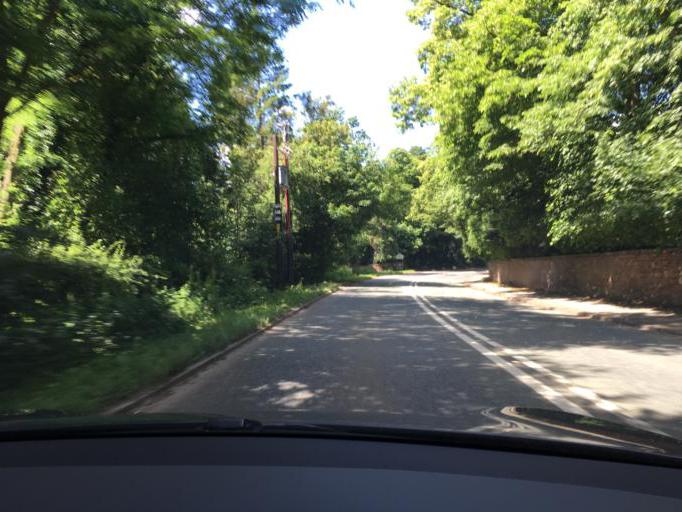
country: GB
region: England
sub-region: Cheshire East
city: Knutsford
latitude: 53.2886
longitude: -2.3447
